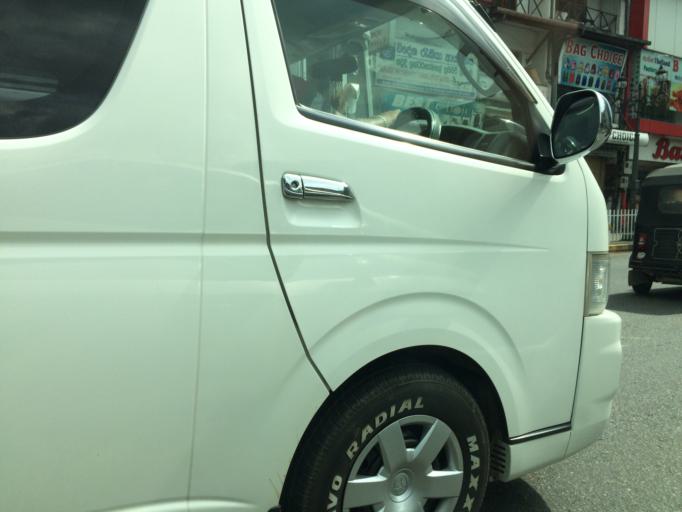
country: LK
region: Central
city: Kandy
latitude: 7.2932
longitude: 80.6356
